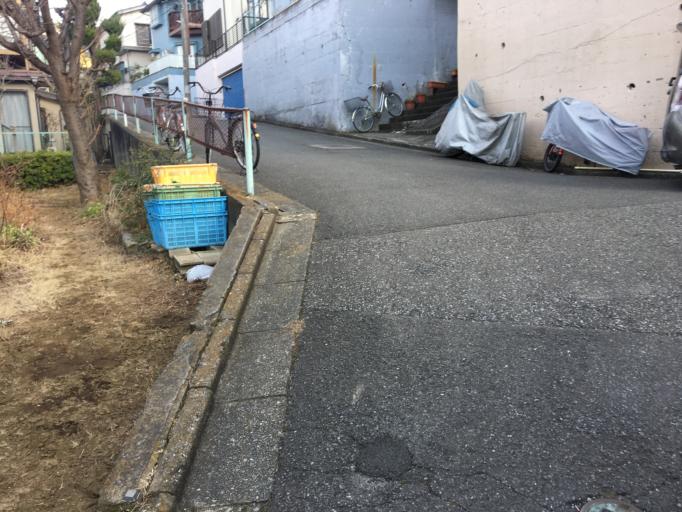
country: JP
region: Saitama
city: Oi
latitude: 35.8435
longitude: 139.5480
